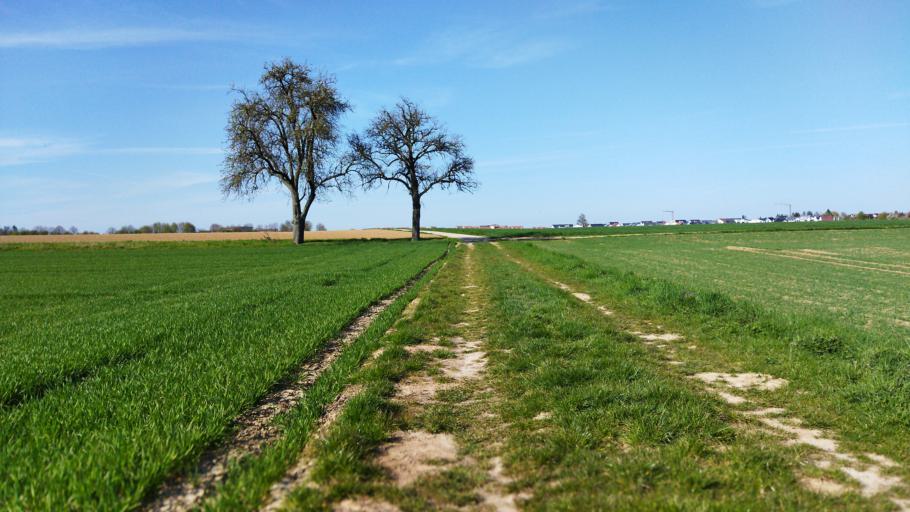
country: DE
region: Baden-Wuerttemberg
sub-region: Regierungsbezirk Stuttgart
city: Bad Wimpfen
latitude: 49.2148
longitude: 9.1474
